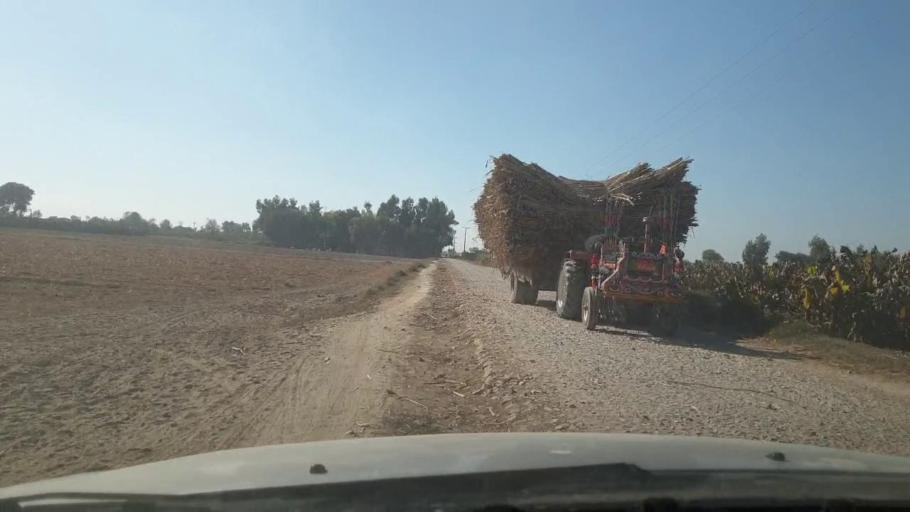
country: PK
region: Sindh
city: Ghotki
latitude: 27.9855
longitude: 69.2251
